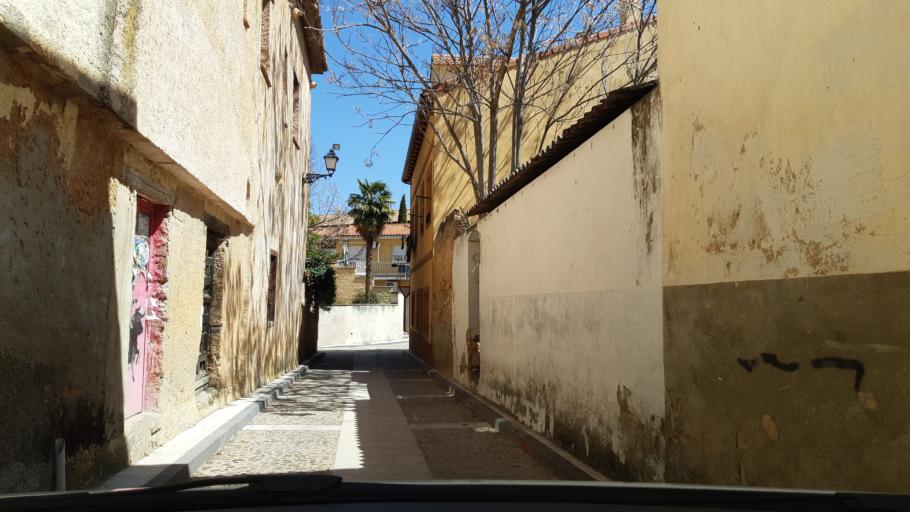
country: ES
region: Castille-La Mancha
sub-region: Provincia de Guadalajara
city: Cifuentes
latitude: 40.7864
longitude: -2.6219
